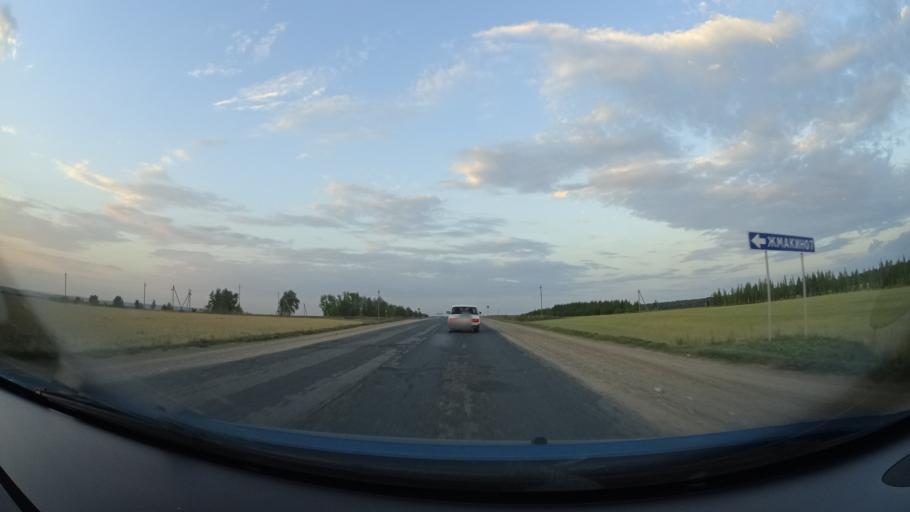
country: RU
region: Tatarstan
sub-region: Bugul'minskiy Rayon
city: Bugul'ma
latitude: 54.2427
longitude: 52.8040
